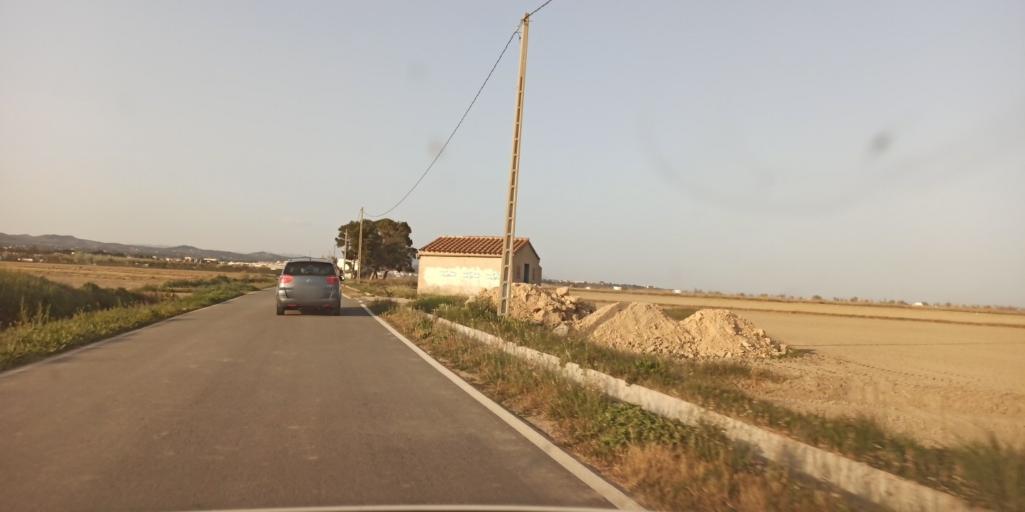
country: ES
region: Catalonia
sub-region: Provincia de Tarragona
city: L'Ampolla
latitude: 40.7914
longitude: 0.6980
